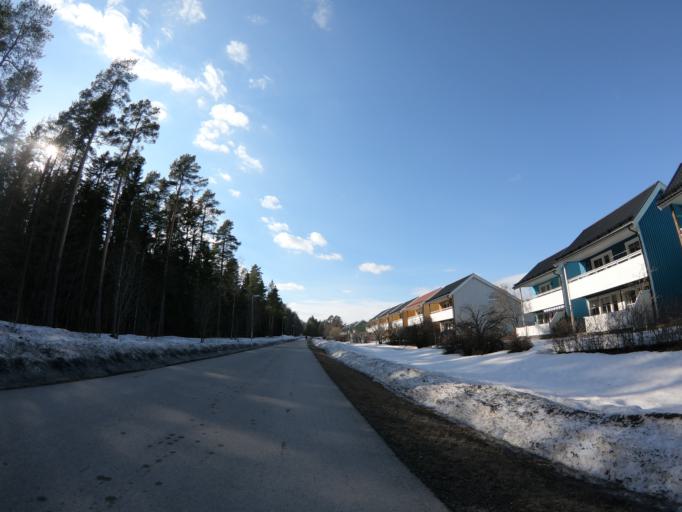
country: SE
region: Vaesterbotten
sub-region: Umea Kommun
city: Ersmark
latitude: 63.8433
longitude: 20.3064
